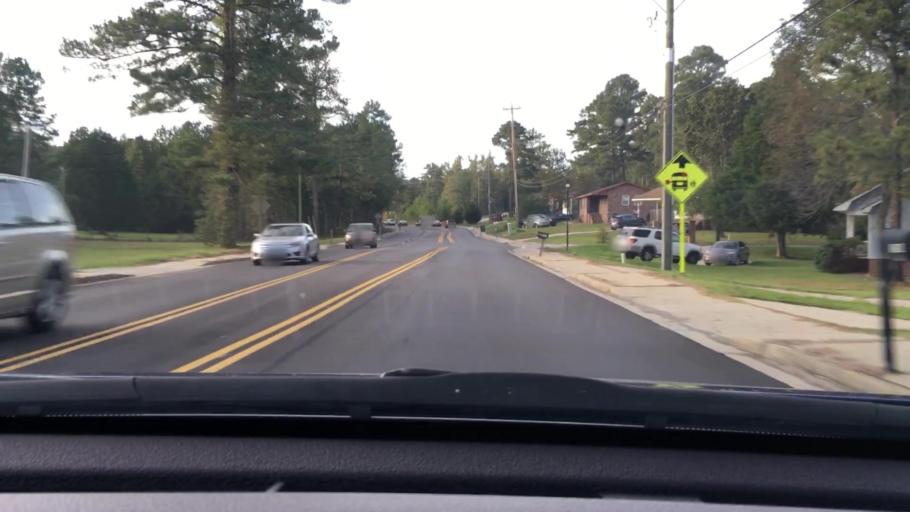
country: US
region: South Carolina
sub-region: Lexington County
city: Irmo
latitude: 34.1118
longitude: -81.1618
